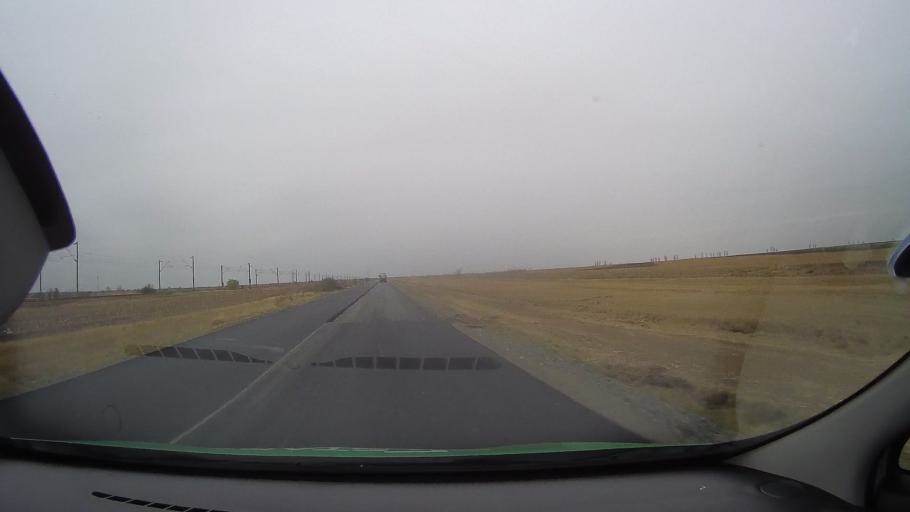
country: RO
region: Braila
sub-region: Comuna Baraganul
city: Baraganul
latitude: 44.7929
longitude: 27.5337
